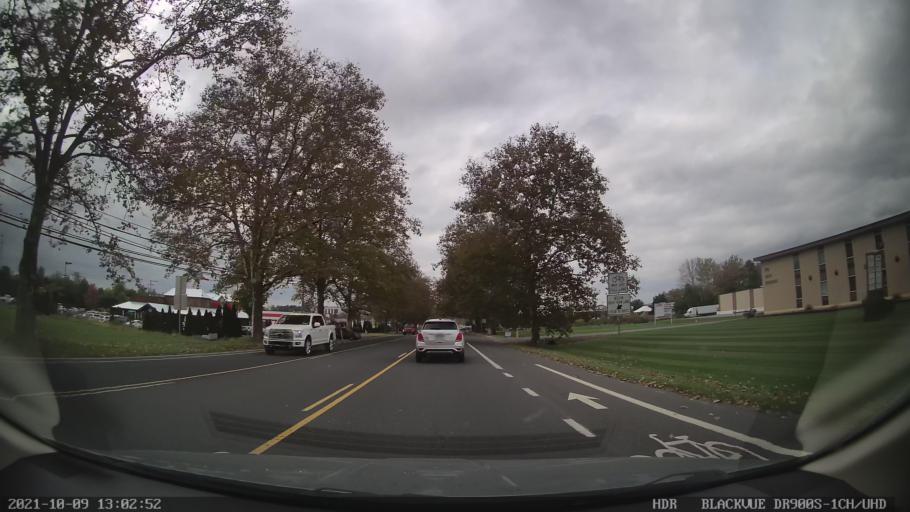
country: US
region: Pennsylvania
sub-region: Lehigh County
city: Ancient Oaks
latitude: 40.5566
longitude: -75.5781
